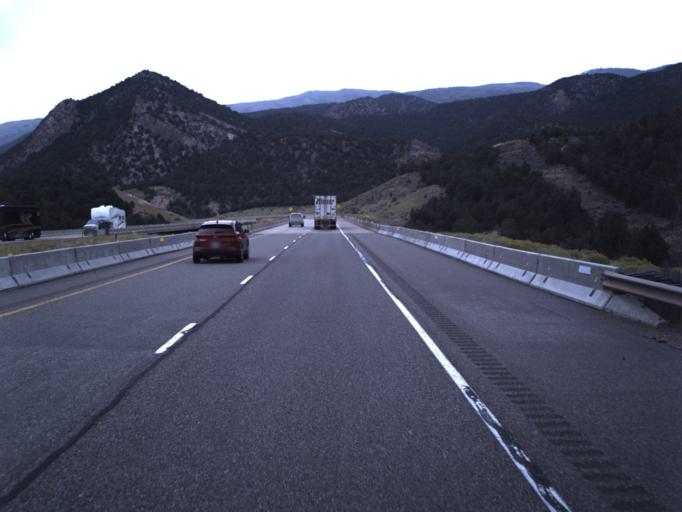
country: US
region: Utah
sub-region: Sevier County
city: Monroe
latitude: 38.5484
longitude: -112.3824
